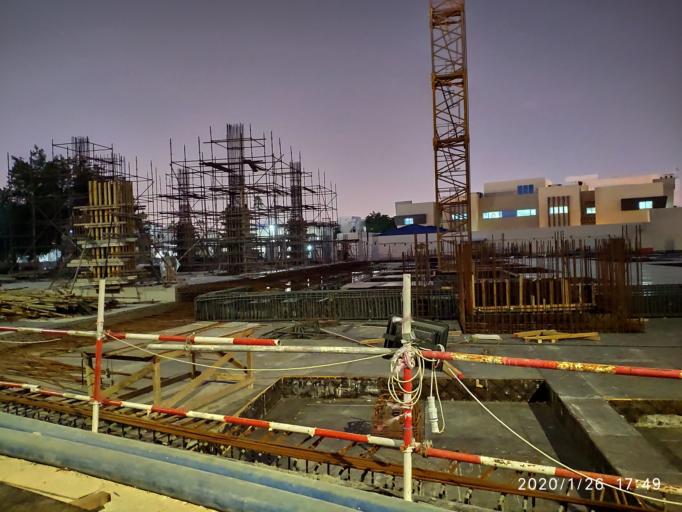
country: QA
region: Baladiyat ad Dawhah
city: Doha
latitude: 25.3177
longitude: 51.5173
